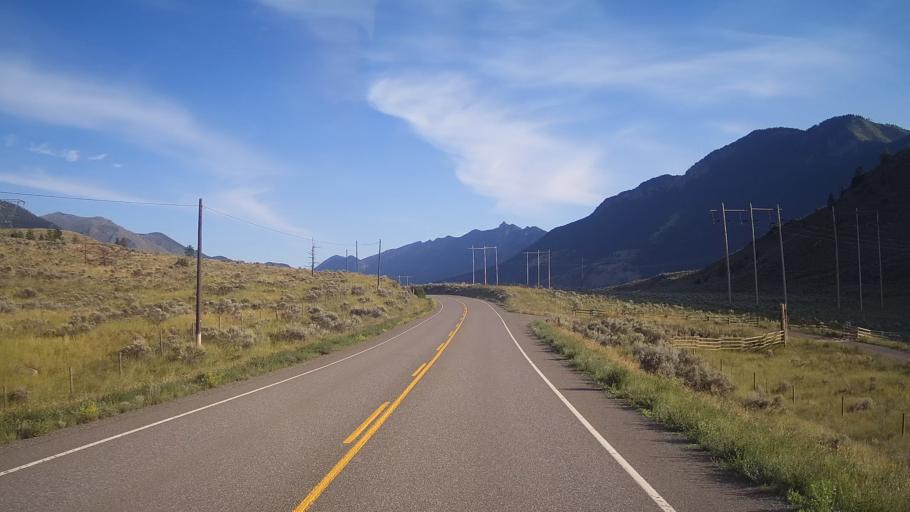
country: CA
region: British Columbia
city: Lillooet
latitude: 50.8229
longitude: -121.8564
